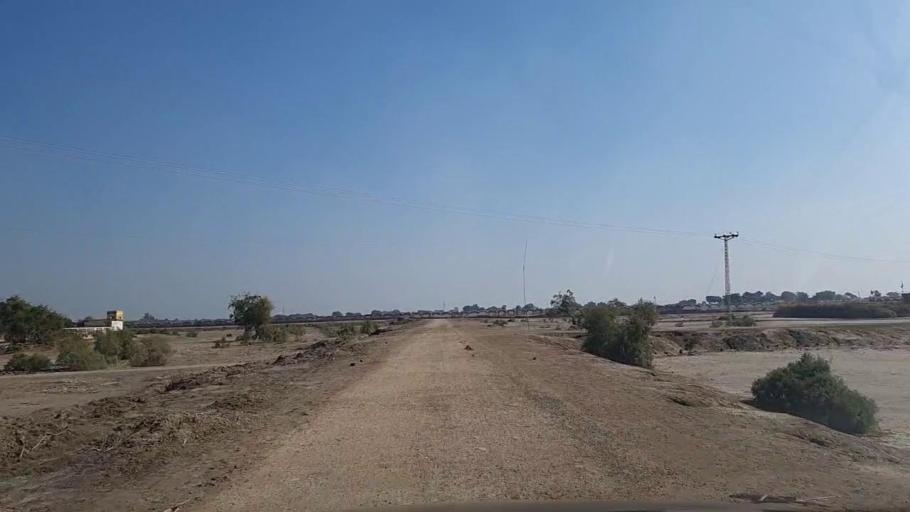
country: PK
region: Sindh
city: Nawabshah
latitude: 26.3187
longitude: 68.3483
